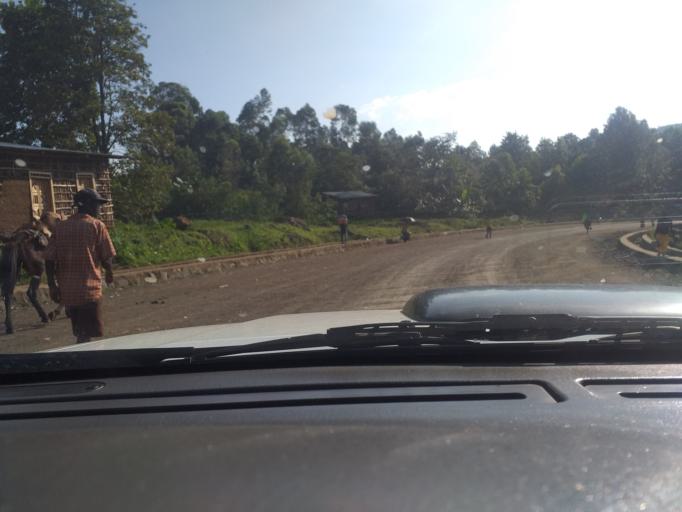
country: ET
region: Southern Nations, Nationalities, and People's Region
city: Bako
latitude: 5.9793
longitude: 36.5724
